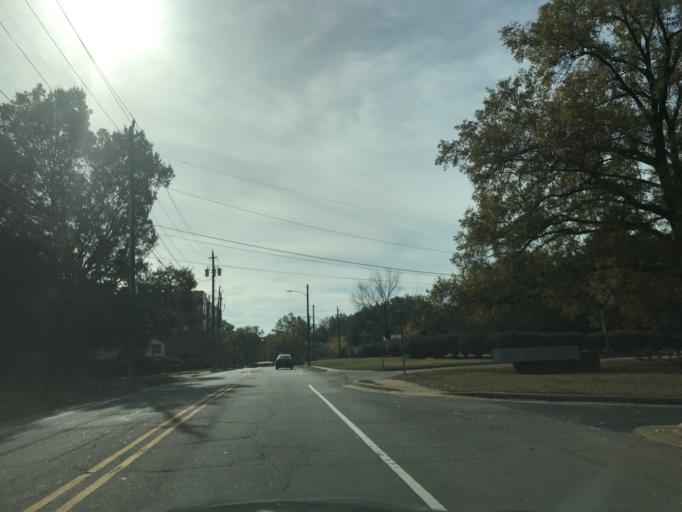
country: US
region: North Carolina
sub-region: Wake County
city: West Raleigh
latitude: 35.7946
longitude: -78.6617
